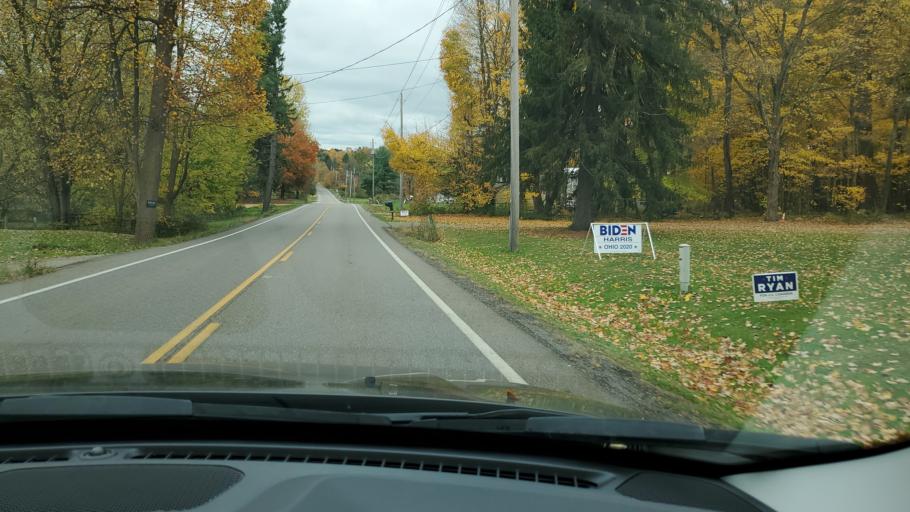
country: US
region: Ohio
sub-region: Mahoning County
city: Boardman
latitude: 40.9493
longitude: -80.6403
